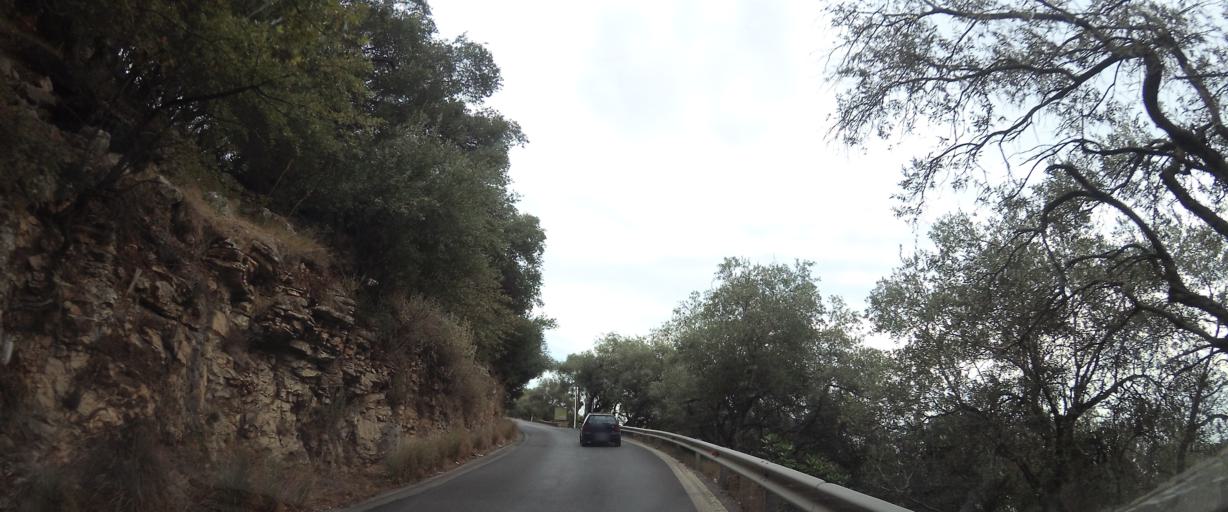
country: GR
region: Ionian Islands
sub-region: Nomos Kerkyras
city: Kontokali
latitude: 39.7349
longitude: 19.9199
